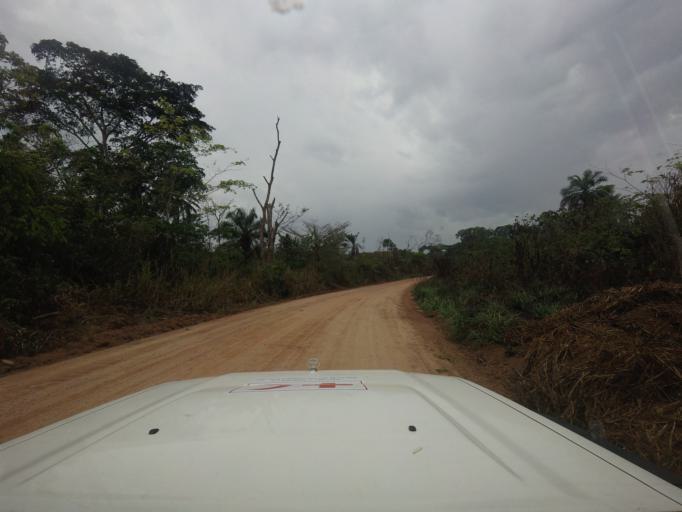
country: SL
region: Eastern Province
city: Buedu
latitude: 8.3057
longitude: -10.1371
